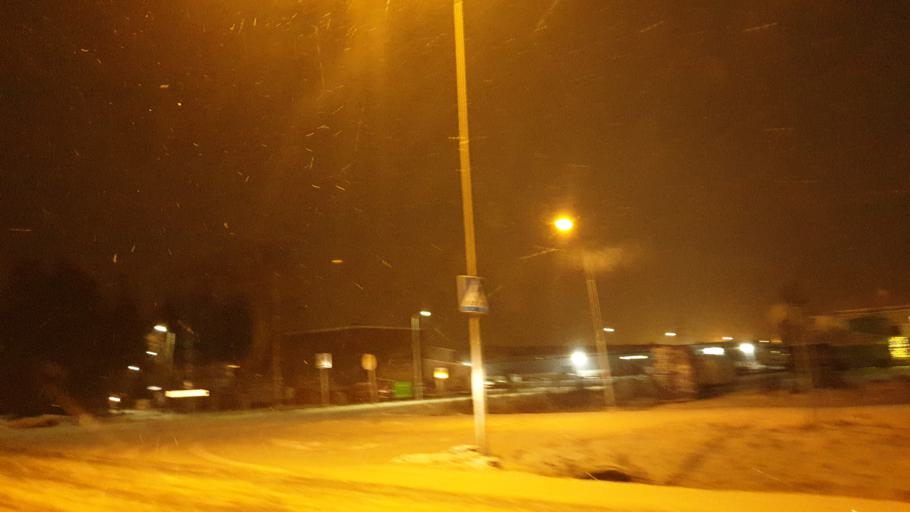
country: FI
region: Northern Ostrobothnia
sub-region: Oulu
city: Oulu
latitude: 64.9938
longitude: 25.4495
